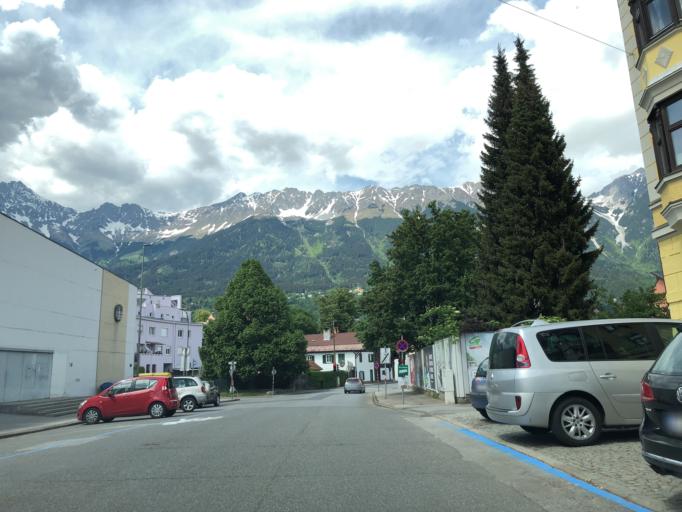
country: AT
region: Tyrol
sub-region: Innsbruck Stadt
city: Innsbruck
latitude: 47.2672
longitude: 11.4084
